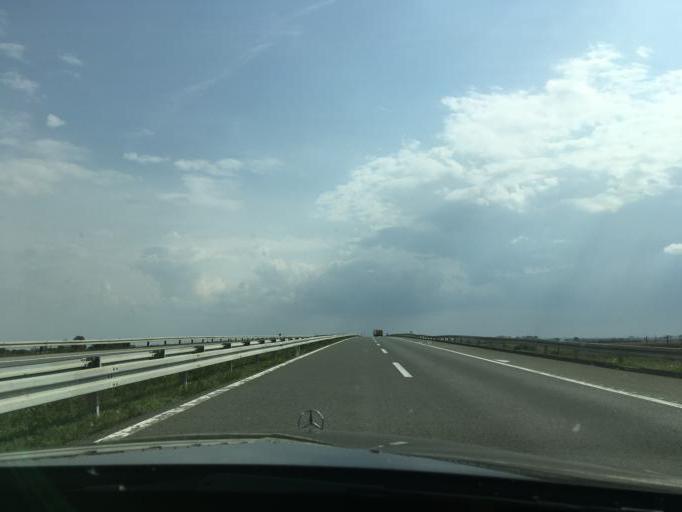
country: RS
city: Sasinci
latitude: 44.9906
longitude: 19.7069
